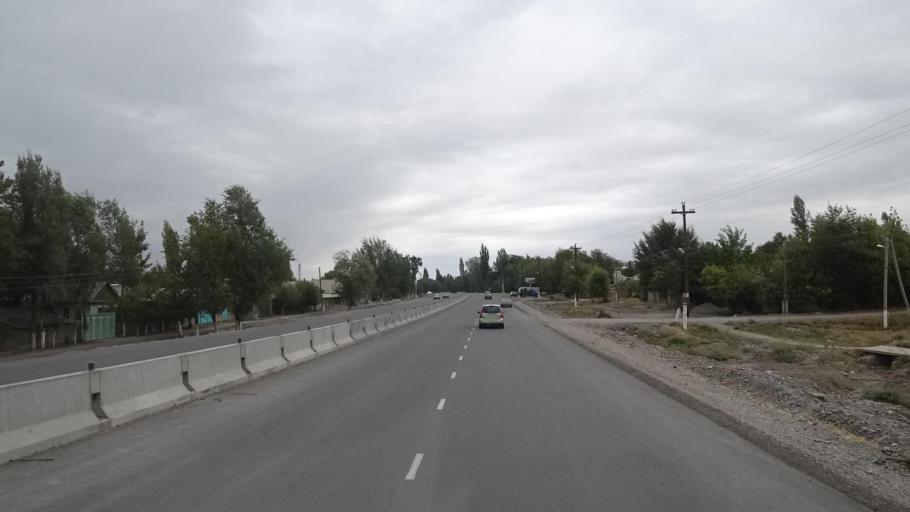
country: KG
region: Chuy
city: Kara-Balta
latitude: 42.8310
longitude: 73.8949
